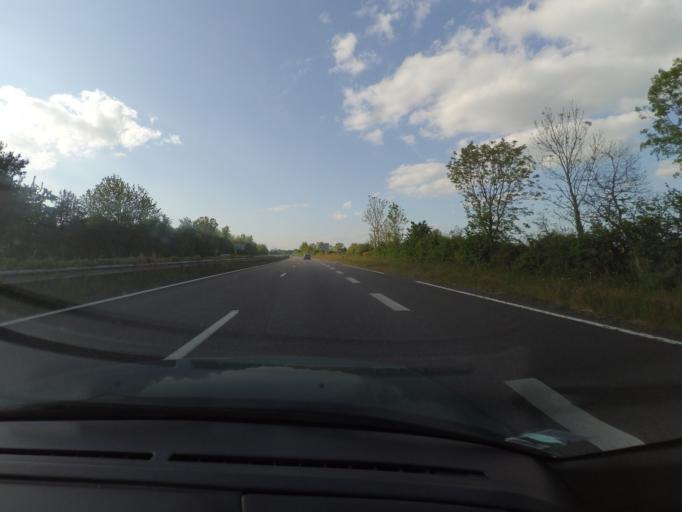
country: FR
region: Pays de la Loire
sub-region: Departement de la Vendee
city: Belleville-sur-Vie
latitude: 46.7842
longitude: -1.4206
